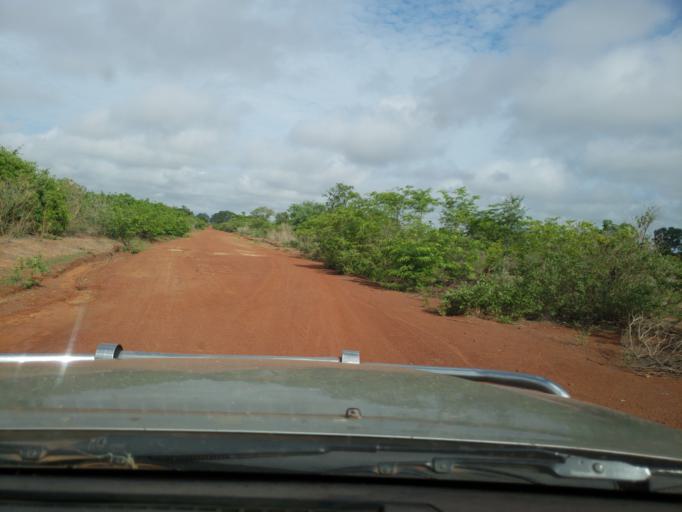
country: ML
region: Sikasso
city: Koutiala
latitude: 12.3924
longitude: -5.9975
